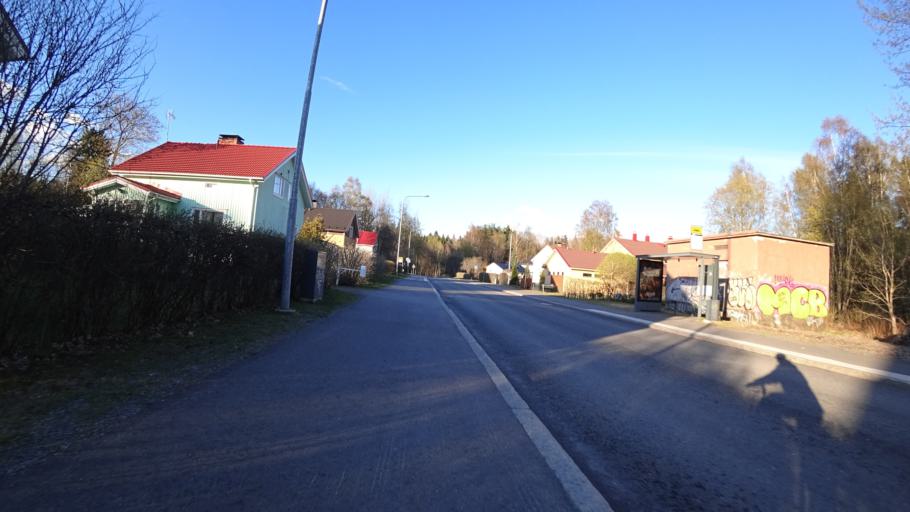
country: FI
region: Pirkanmaa
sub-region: Tampere
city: Pirkkala
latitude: 61.4969
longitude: 23.5871
